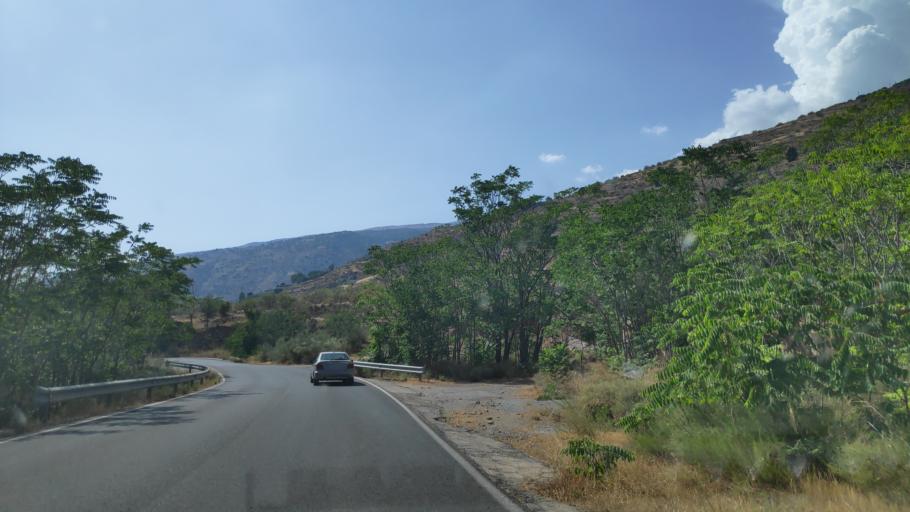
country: ES
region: Andalusia
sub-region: Provincia de Granada
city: Soportujar
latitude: 36.9232
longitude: -3.3912
